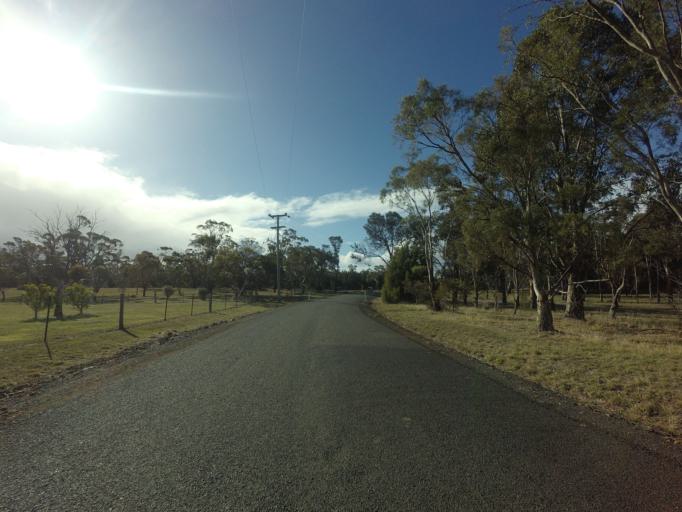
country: AU
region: Tasmania
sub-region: Sorell
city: Sorell
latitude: -42.3061
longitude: 147.9902
